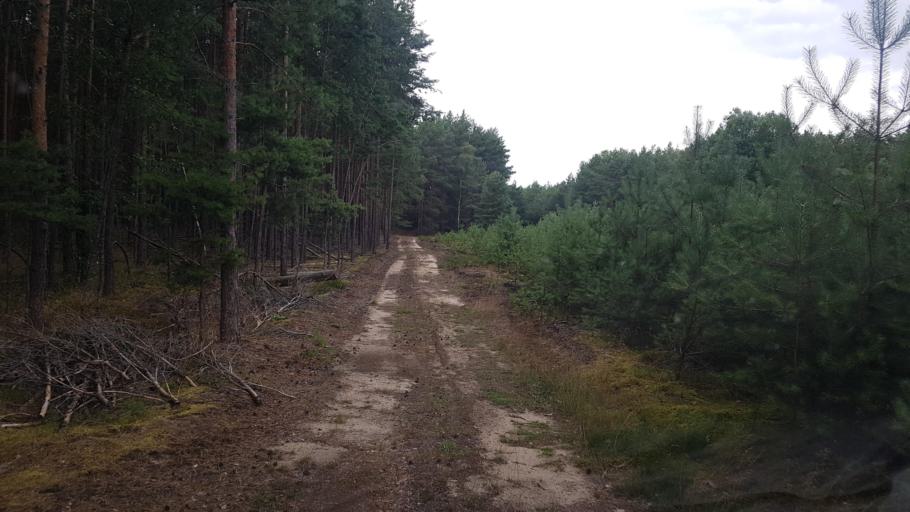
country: DE
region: Brandenburg
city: Crinitz
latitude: 51.7222
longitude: 13.7264
